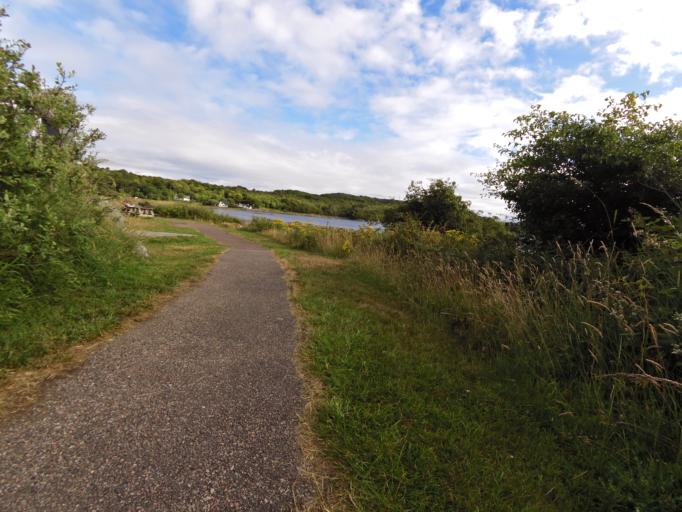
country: GB
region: Scotland
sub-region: Argyll and Bute
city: Isle Of Mull
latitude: 56.9099
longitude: -5.8476
